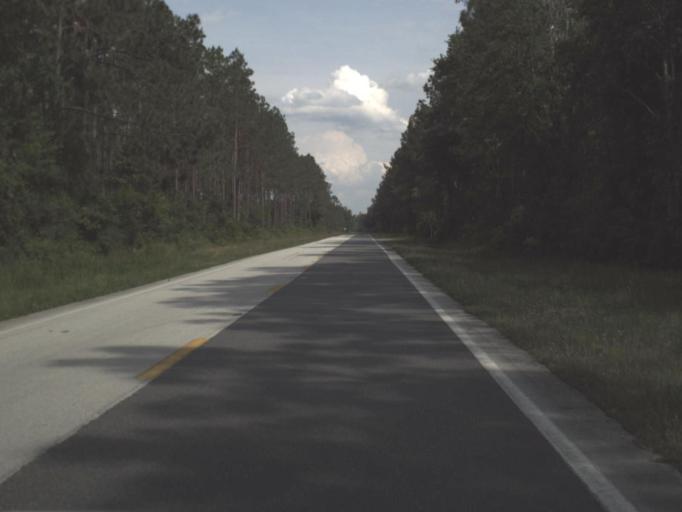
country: US
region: Florida
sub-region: Columbia County
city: Five Points
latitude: 30.5792
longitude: -82.4629
